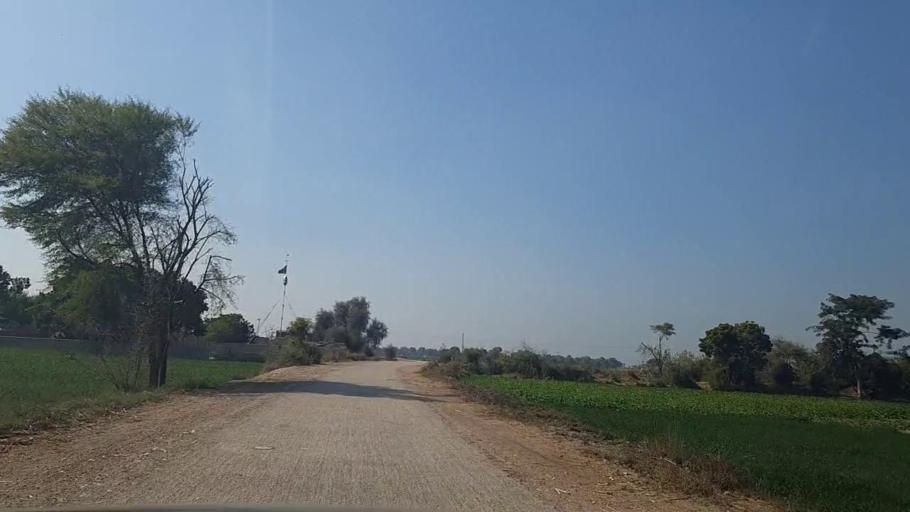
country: PK
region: Sindh
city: Daulatpur
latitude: 26.2846
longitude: 68.0476
